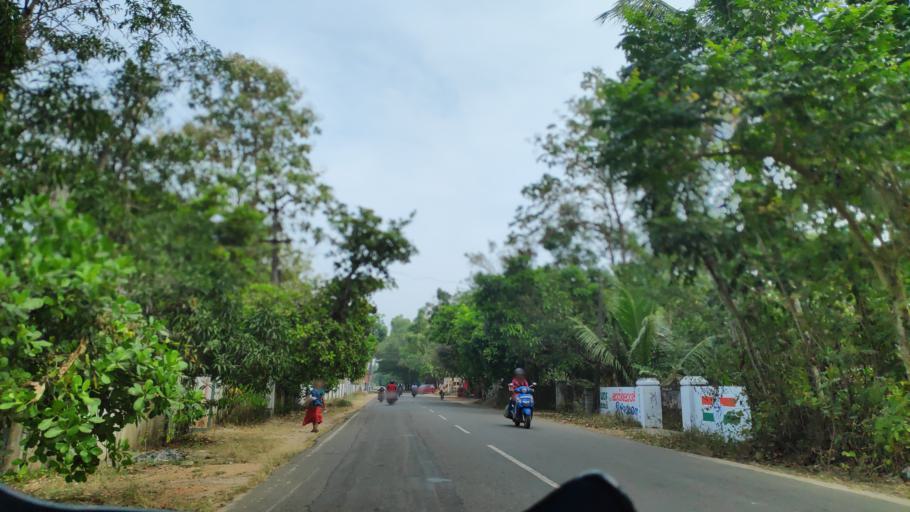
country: IN
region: Kerala
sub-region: Kottayam
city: Vaikam
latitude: 9.7426
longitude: 76.3630
